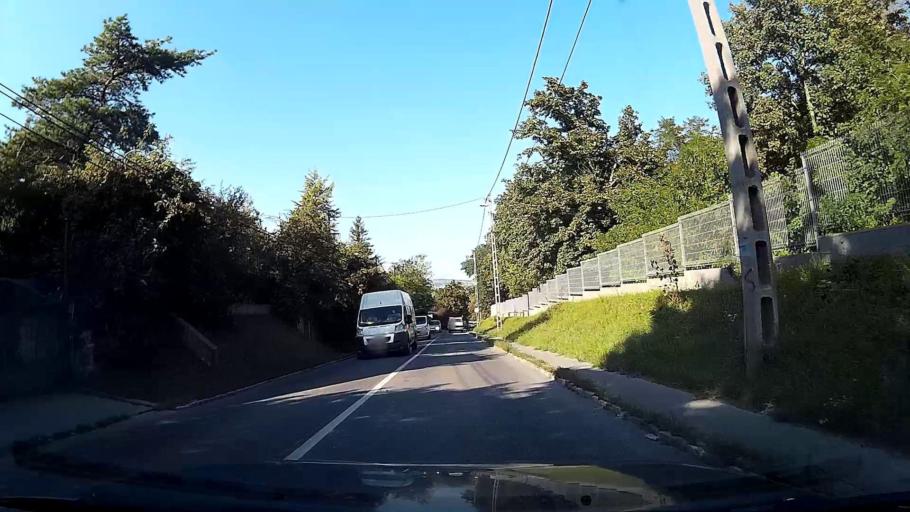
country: HU
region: Pest
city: Budaors
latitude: 47.4366
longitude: 18.9786
